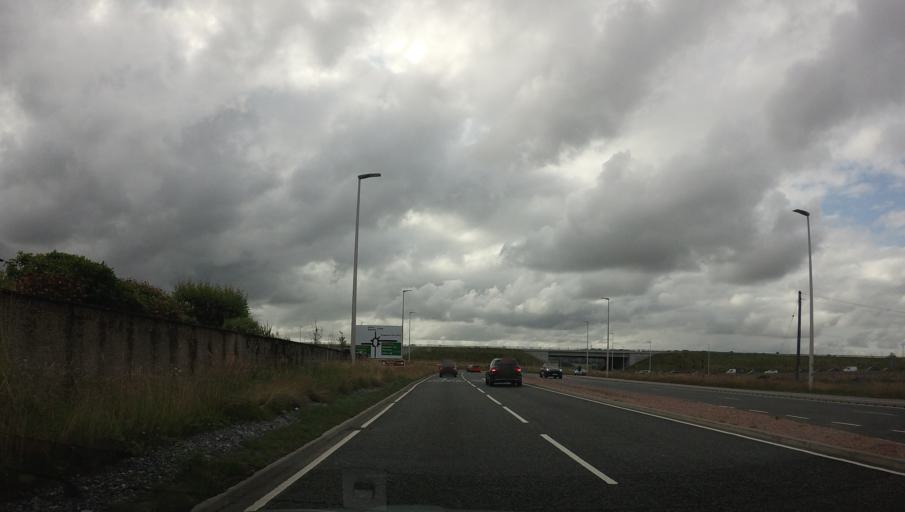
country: GB
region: Scotland
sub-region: Aberdeenshire
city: Westhill
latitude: 57.1470
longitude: -2.2396
